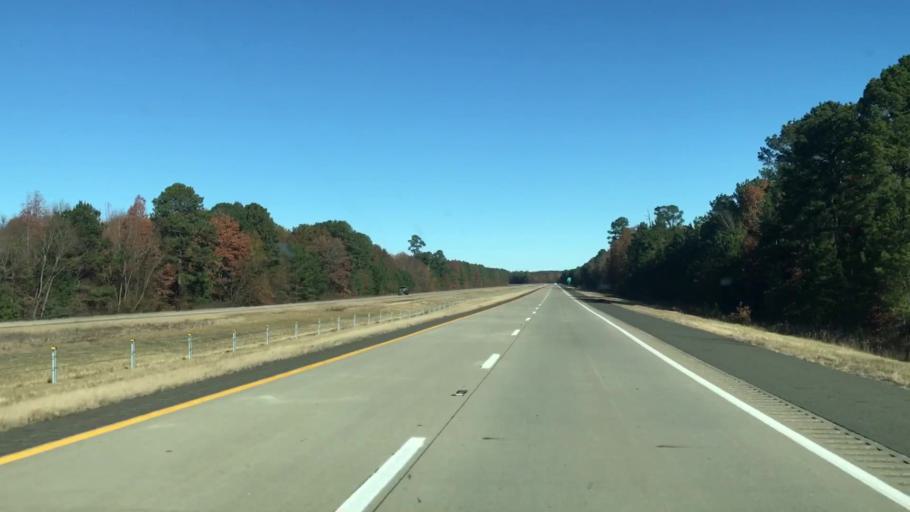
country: US
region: Texas
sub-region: Bowie County
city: Texarkana
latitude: 33.2281
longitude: -93.8731
